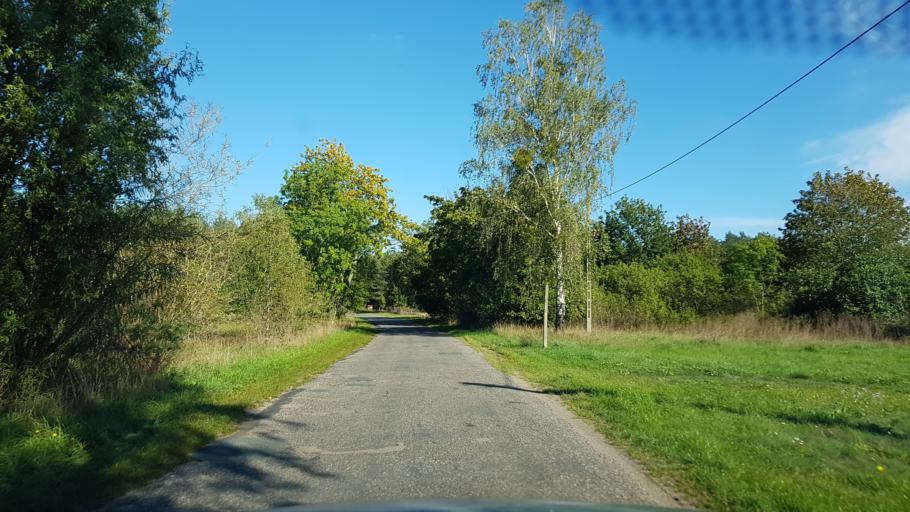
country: PL
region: West Pomeranian Voivodeship
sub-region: Powiat mysliborski
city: Nowogrodek Pomorski
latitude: 52.8688
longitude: 14.9750
